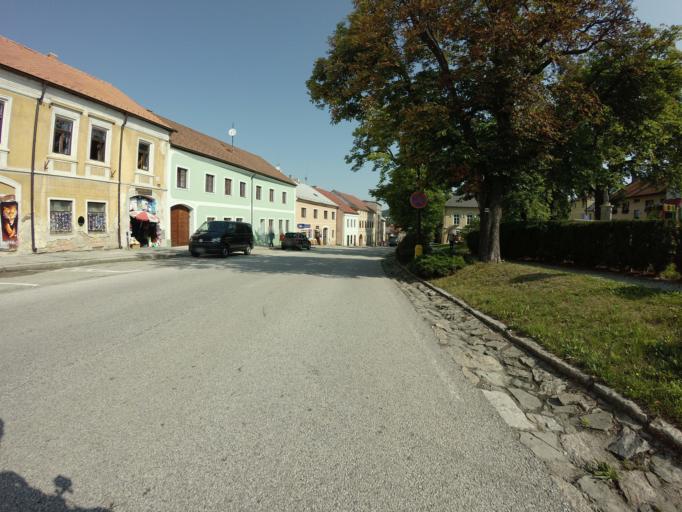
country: CZ
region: Jihocesky
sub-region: Okres Cesky Krumlov
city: Vyssi Brod
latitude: 48.6141
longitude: 14.3114
